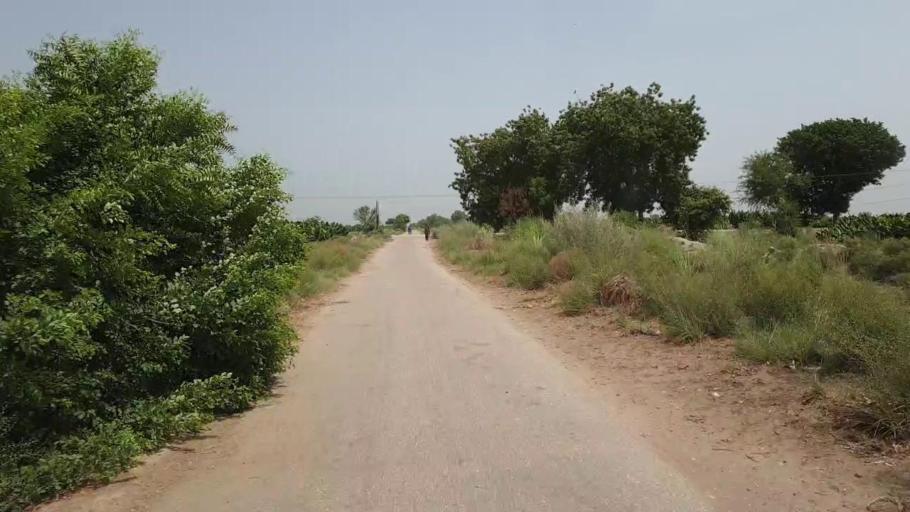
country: PK
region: Sindh
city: Nawabshah
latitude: 26.2824
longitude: 68.3114
